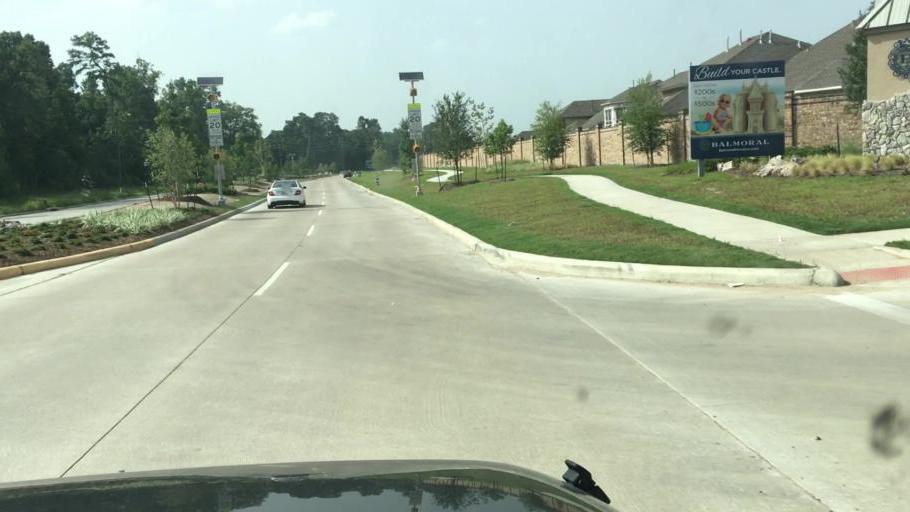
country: US
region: Texas
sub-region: Harris County
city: Atascocita
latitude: 29.9439
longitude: -95.2113
